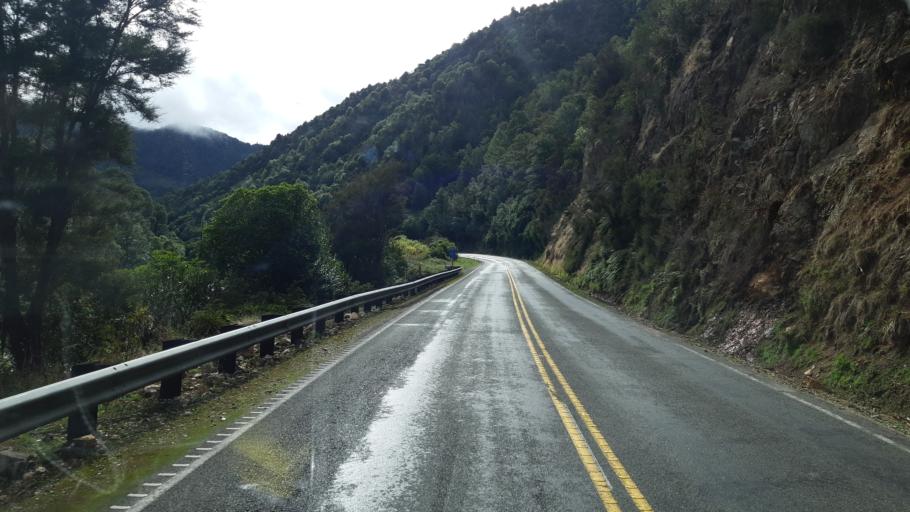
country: NZ
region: West Coast
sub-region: Buller District
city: Westport
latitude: -41.7745
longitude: 172.2244
